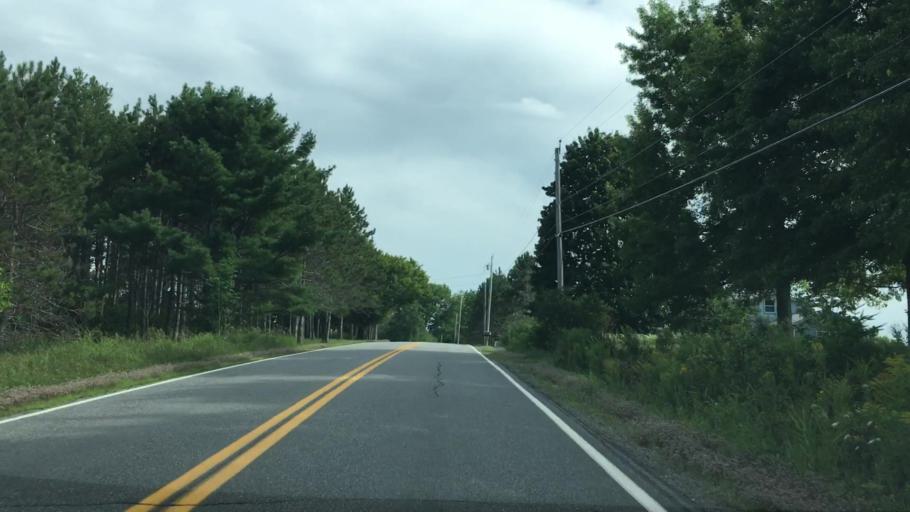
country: US
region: Maine
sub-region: Waldo County
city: Belfast
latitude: 44.3797
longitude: -69.0344
